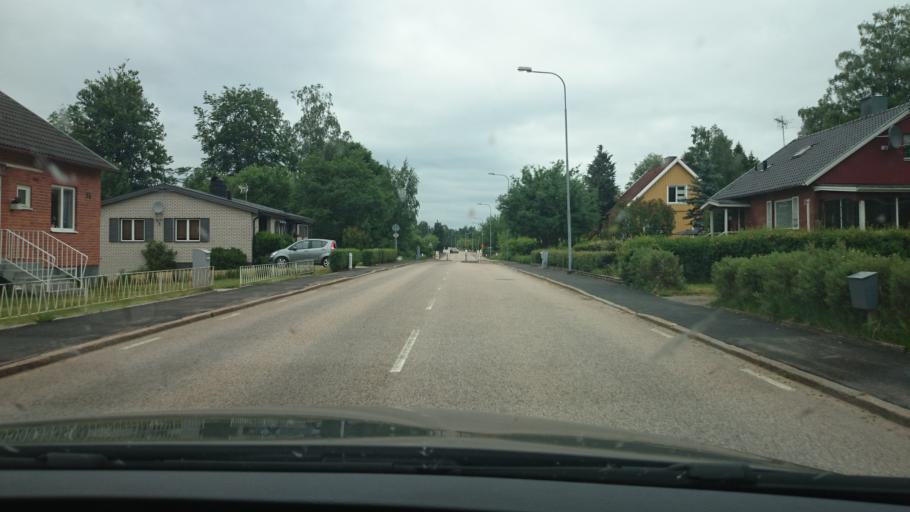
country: SE
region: Halland
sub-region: Hylte Kommun
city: Hyltebruk
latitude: 56.9921
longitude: 13.2303
